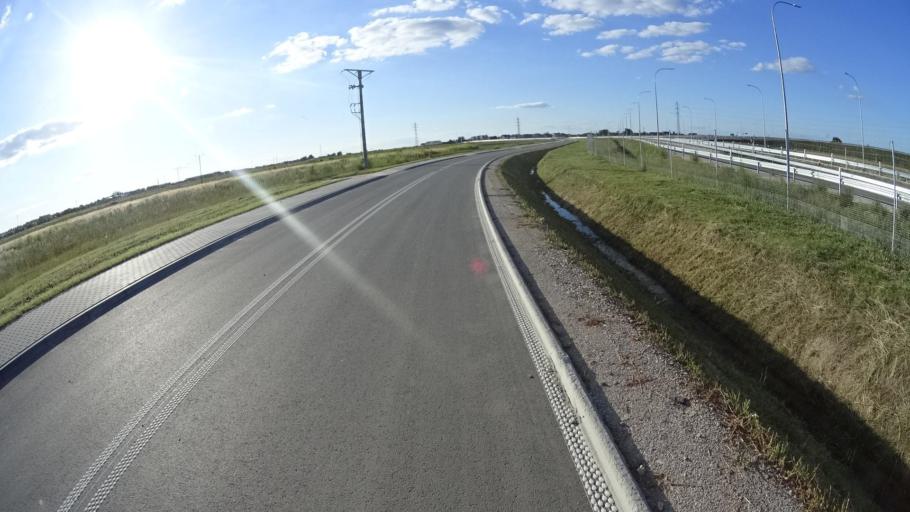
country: PL
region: Masovian Voivodeship
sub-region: Powiat piaseczynski
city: Lesznowola
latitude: 52.0874
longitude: 20.9662
